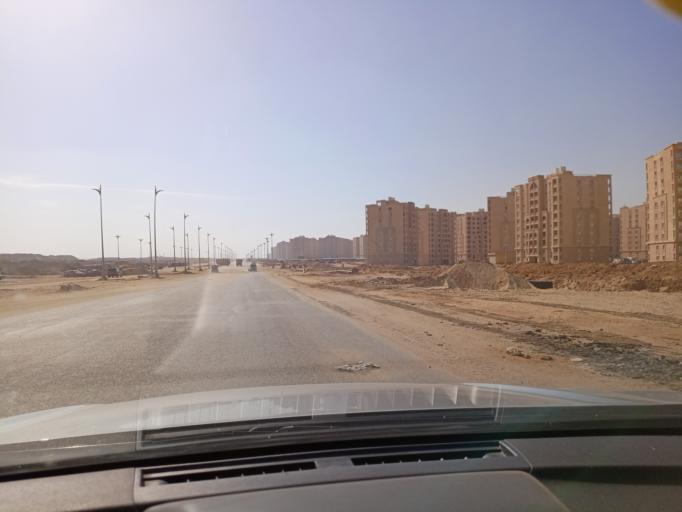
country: EG
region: Muhafazat al Qalyubiyah
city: Al Khankah
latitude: 30.0235
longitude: 31.6688
